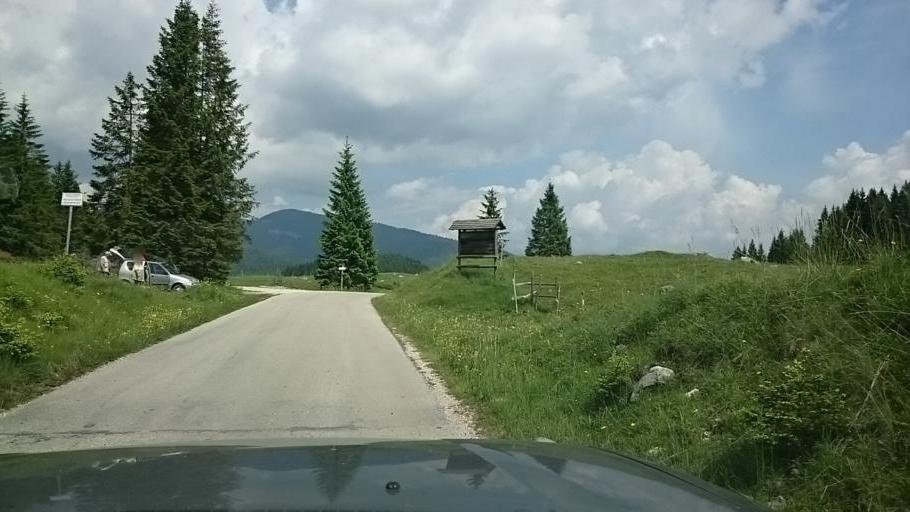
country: IT
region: Trentino-Alto Adige
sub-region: Provincia di Trento
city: Grigno
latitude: 45.9715
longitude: 11.5999
